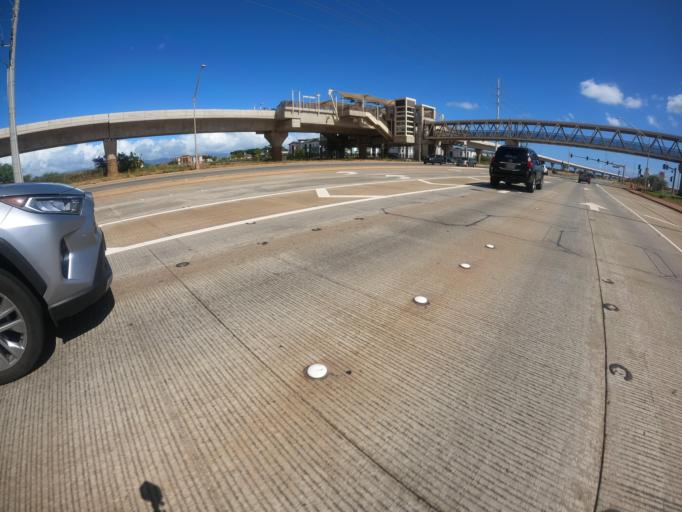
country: US
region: Hawaii
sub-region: Honolulu County
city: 'Ewa Villages
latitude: 21.3587
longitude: -158.0520
